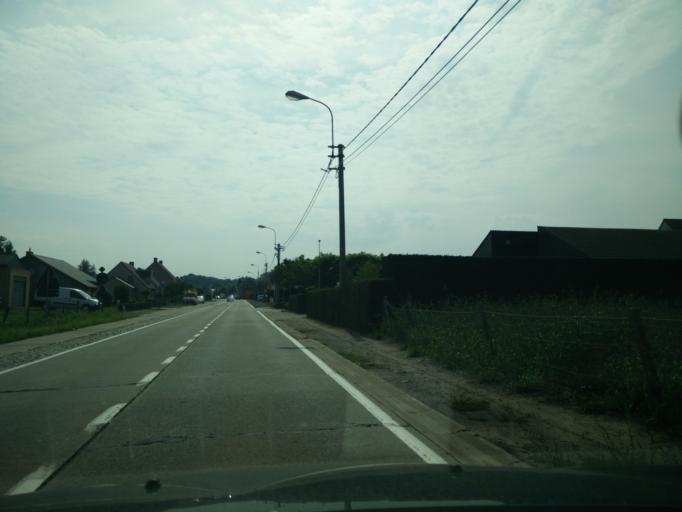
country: BE
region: Flanders
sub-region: Provincie Oost-Vlaanderen
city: Merelbeke
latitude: 50.9701
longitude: 3.7353
